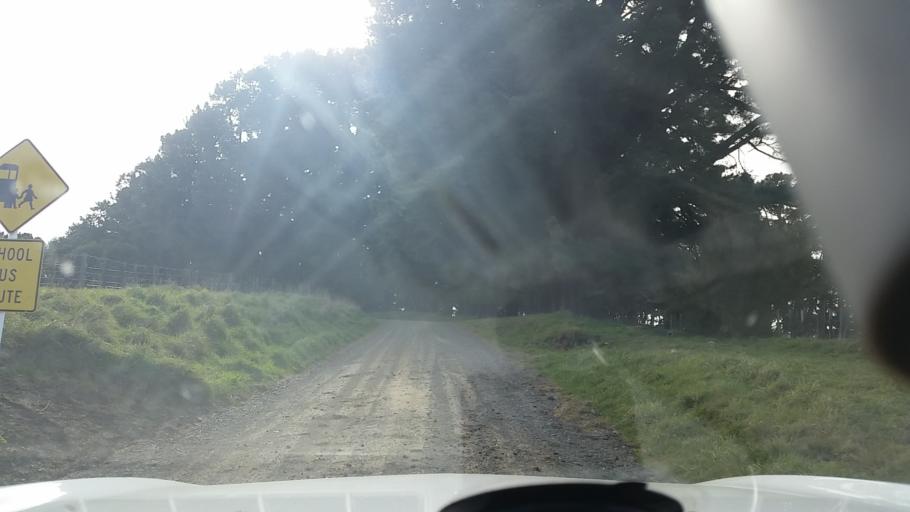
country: NZ
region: Hawke's Bay
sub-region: Napier City
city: Napier
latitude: -39.1349
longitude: 176.9089
